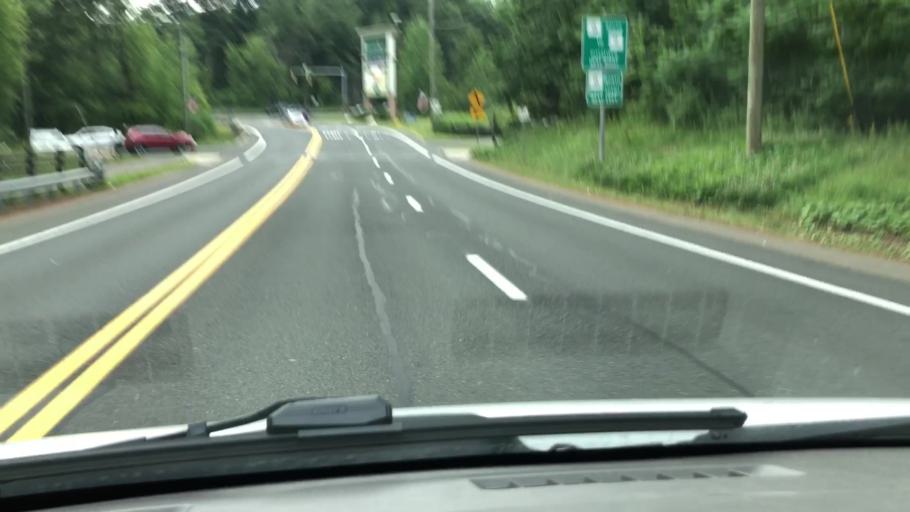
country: US
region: Massachusetts
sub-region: Berkshire County
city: Lanesborough
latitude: 42.4888
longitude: -73.2042
